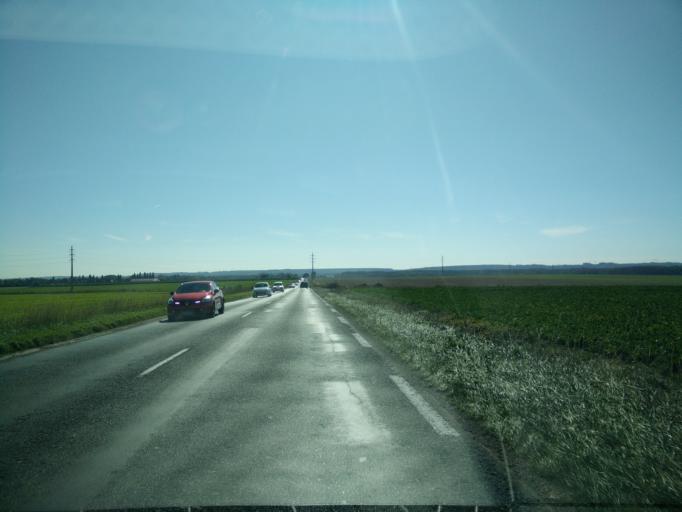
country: FR
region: Ile-de-France
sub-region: Departement de Seine-et-Marne
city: Claye-Souilly
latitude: 48.9783
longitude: 2.6600
